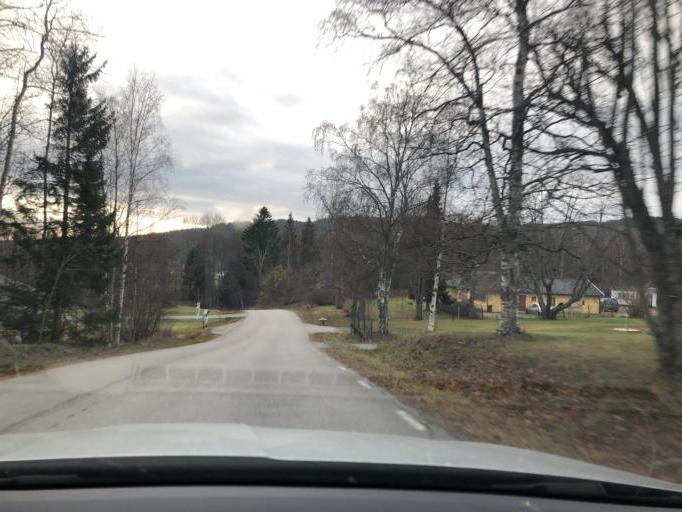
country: SE
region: Gaevleborg
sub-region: Hudiksvalls Kommun
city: Sorforsa
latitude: 61.6801
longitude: 16.9250
